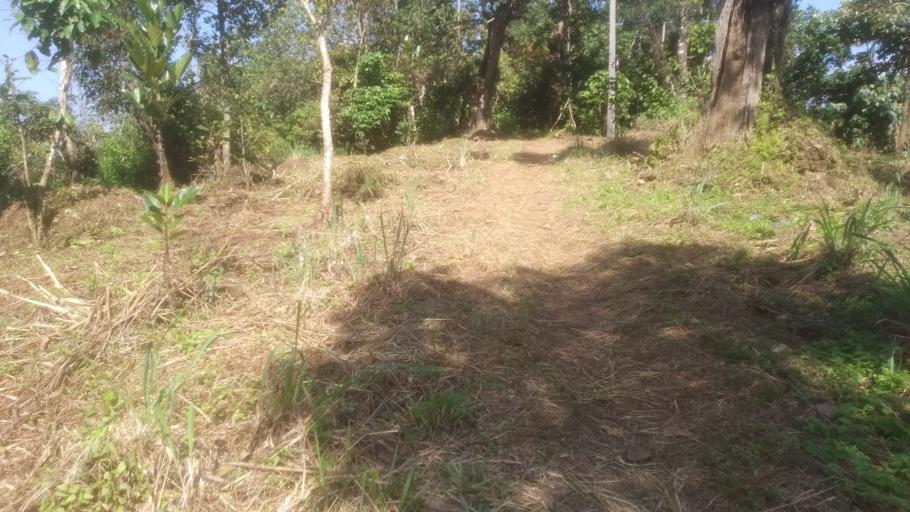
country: IN
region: Kerala
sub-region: Idukki
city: Idukki
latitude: 9.9794
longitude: 76.8337
